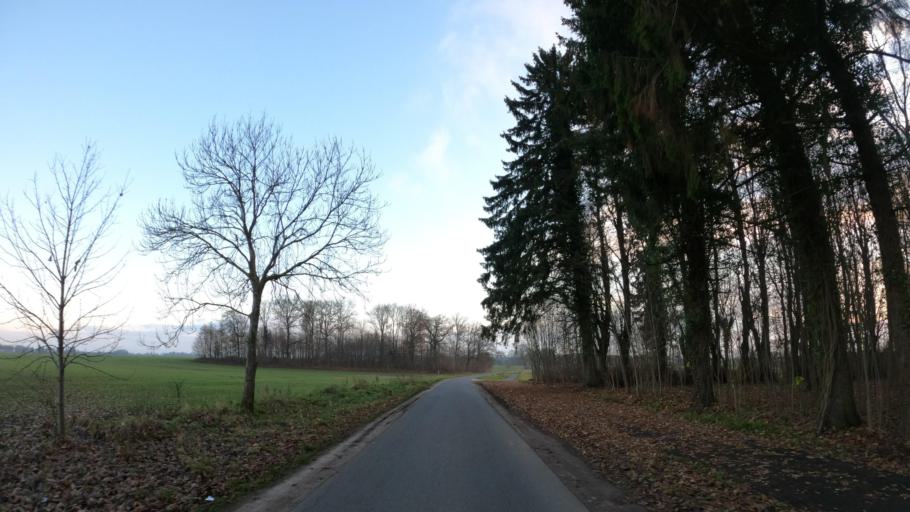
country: PL
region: West Pomeranian Voivodeship
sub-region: Powiat bialogardzki
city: Karlino
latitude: 54.1086
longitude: 15.8859
